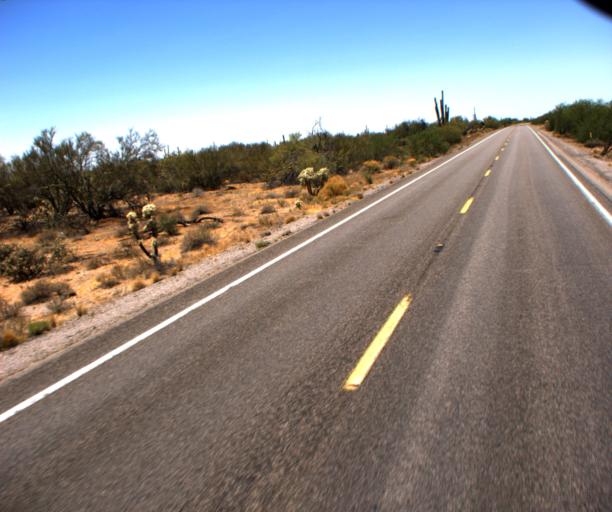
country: US
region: Arizona
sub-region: Pima County
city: Marana
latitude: 32.7652
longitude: -111.1521
